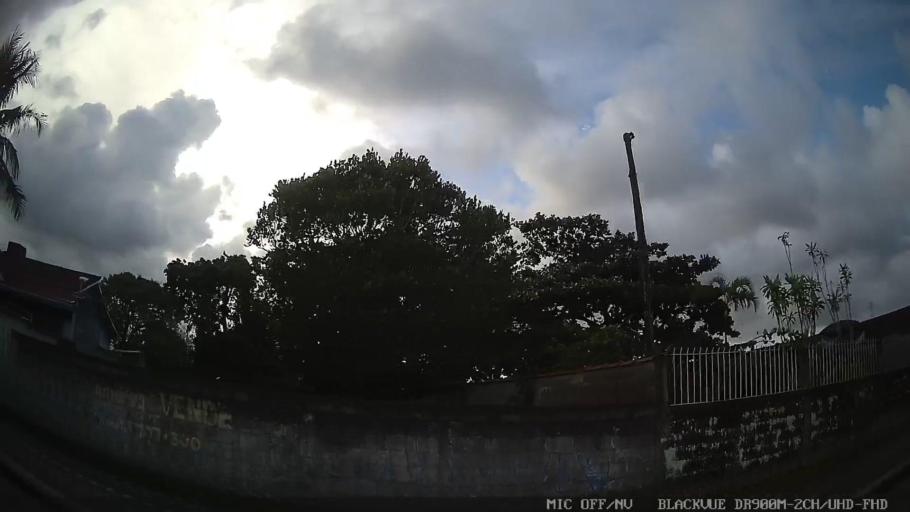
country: BR
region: Sao Paulo
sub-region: Mongagua
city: Mongagua
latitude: -24.1205
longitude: -46.6770
